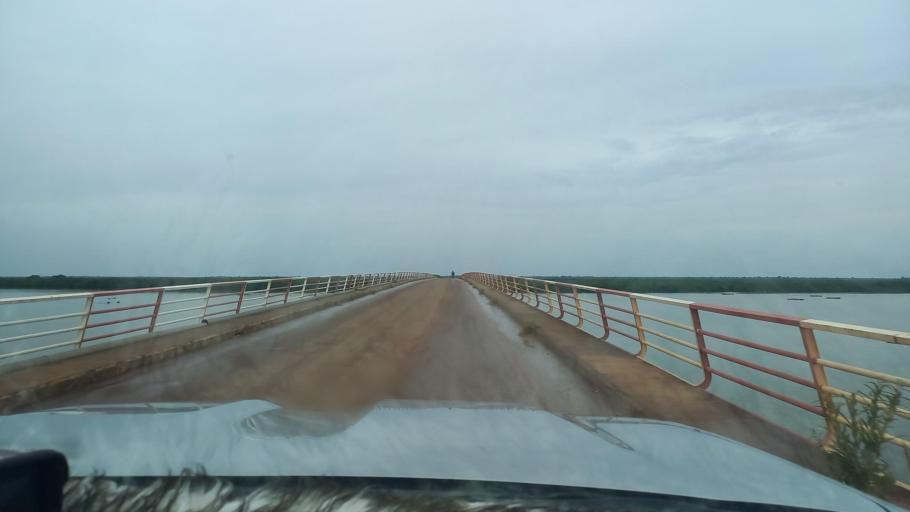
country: SN
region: Ziguinchor
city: Ziguinchor
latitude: 12.5881
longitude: -16.2627
